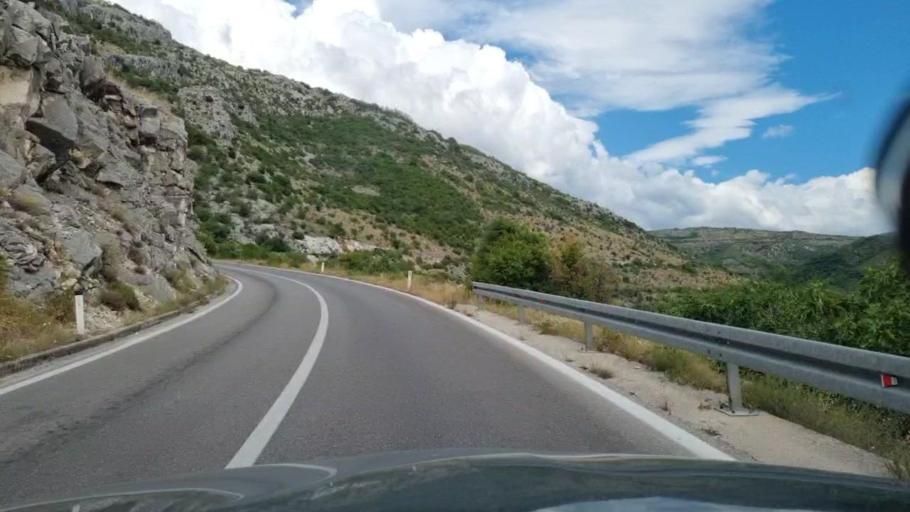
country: BA
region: Federation of Bosnia and Herzegovina
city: Blagaj
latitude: 43.2639
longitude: 17.9058
